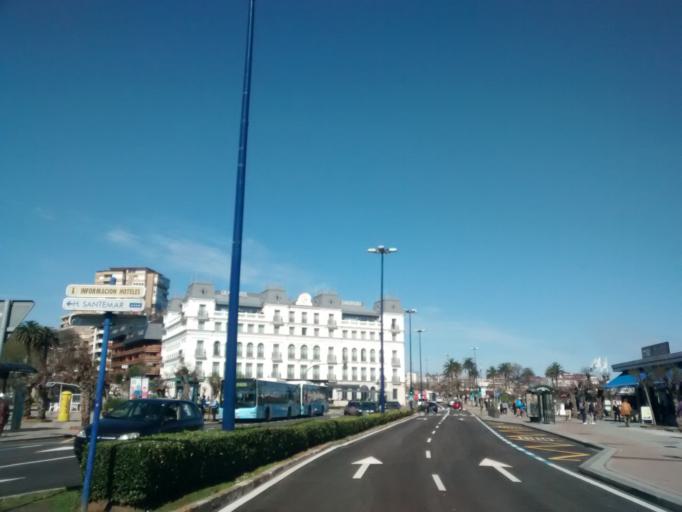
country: ES
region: Cantabria
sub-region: Provincia de Cantabria
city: Santander
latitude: 43.4718
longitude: -3.7817
